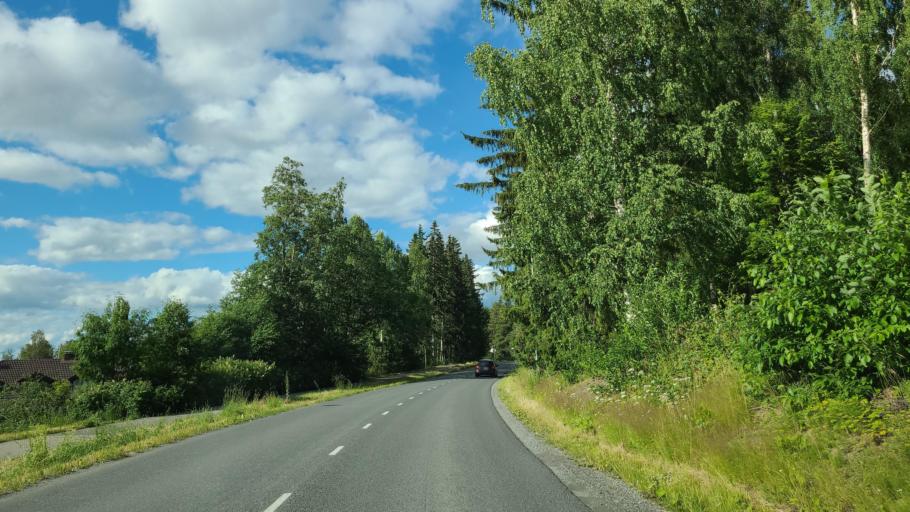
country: FI
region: Northern Savo
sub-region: Kuopio
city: Kuopio
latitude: 62.9347
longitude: 27.6335
